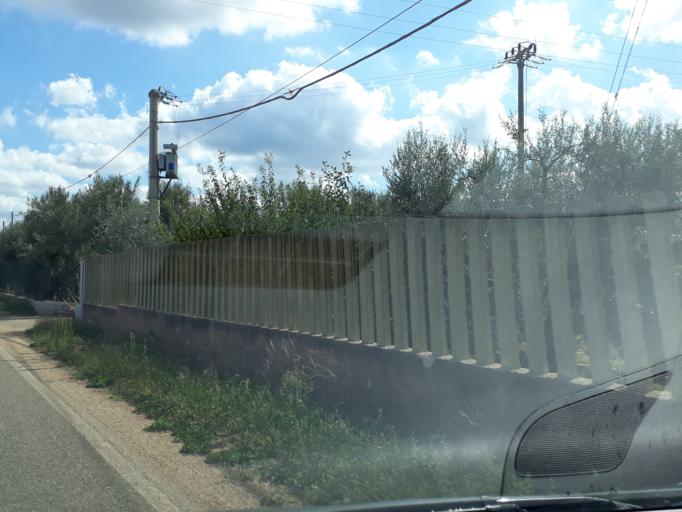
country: IT
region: Apulia
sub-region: Provincia di Brindisi
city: Pezze di Greco
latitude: 40.8024
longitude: 17.3973
